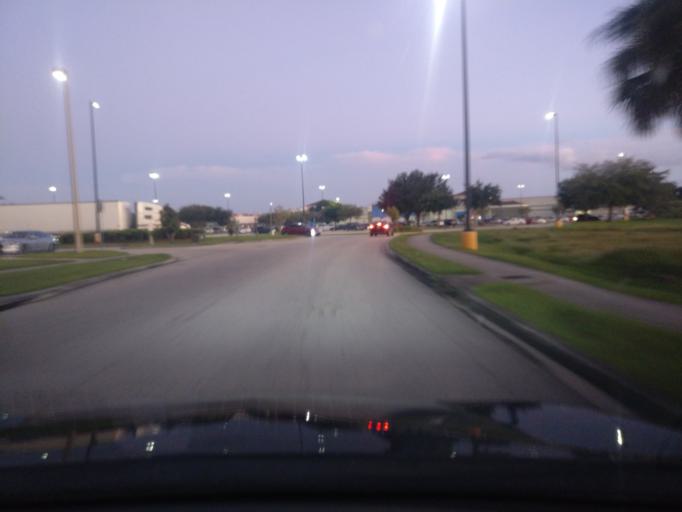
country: US
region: Florida
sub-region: Osceola County
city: Celebration
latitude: 28.3440
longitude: -81.4877
